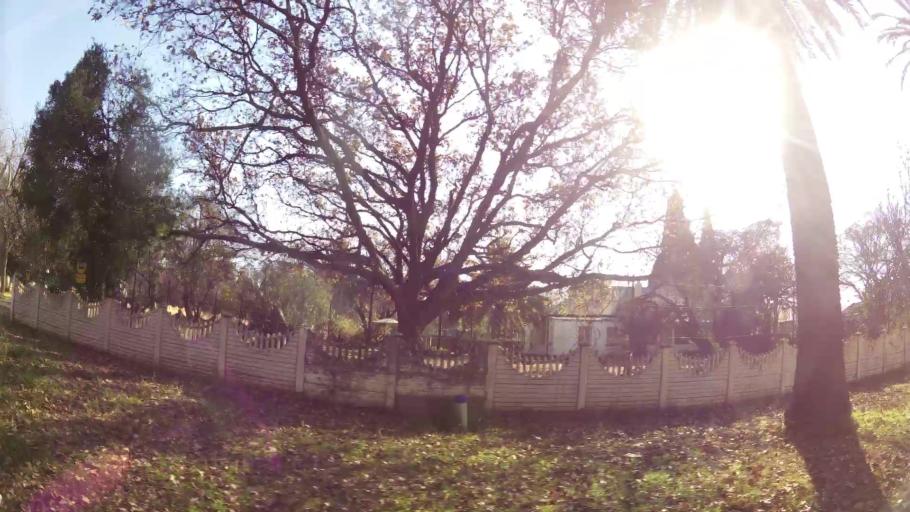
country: ZA
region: Gauteng
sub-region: Ekurhuleni Metropolitan Municipality
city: Boksburg
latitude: -26.2166
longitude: 28.2392
